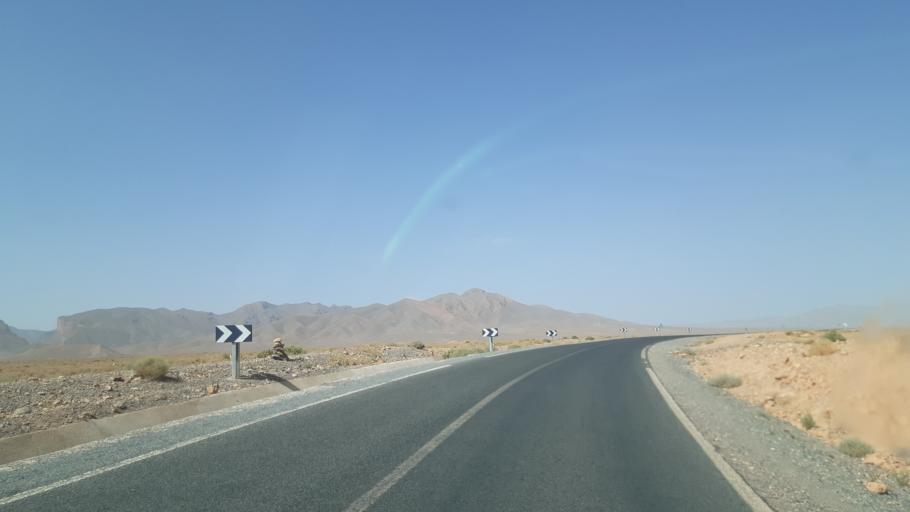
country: MA
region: Meknes-Tafilalet
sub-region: Errachidia
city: Amouguer
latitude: 32.2311
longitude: -4.6491
